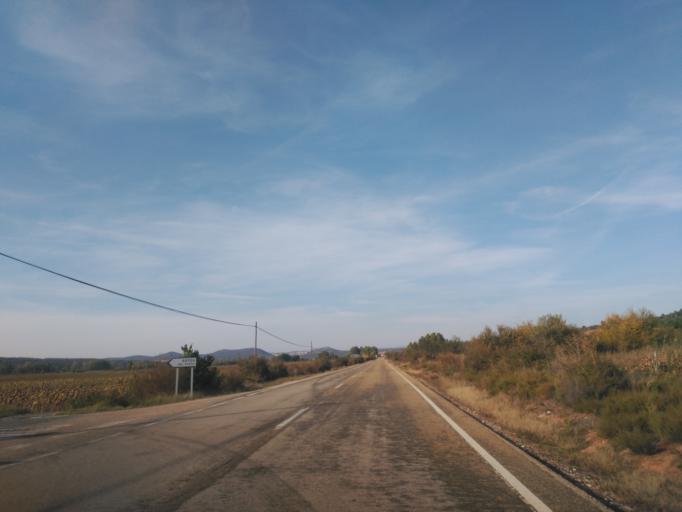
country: ES
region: Castille and Leon
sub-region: Provincia de Soria
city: Valdemaluque
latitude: 41.6593
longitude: -3.0506
